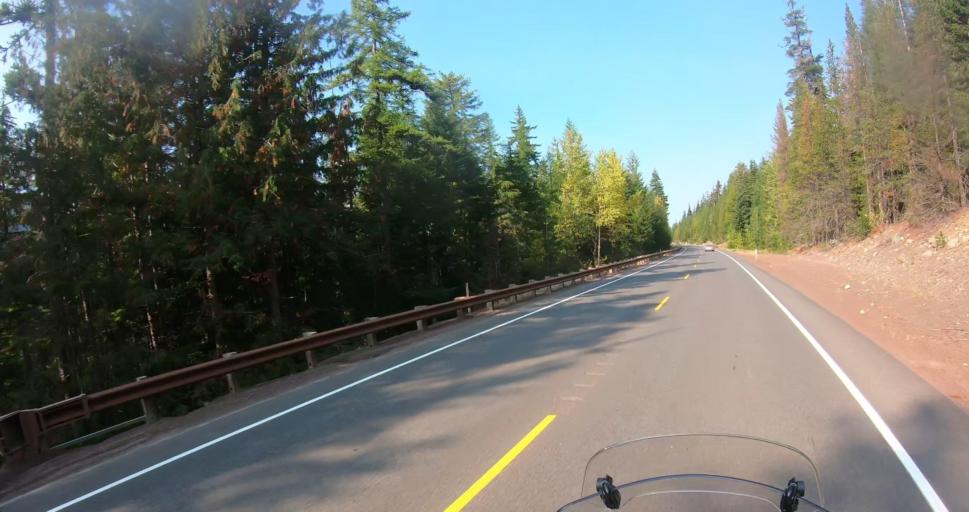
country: US
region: Oregon
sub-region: Hood River County
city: Odell
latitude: 45.3417
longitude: -121.5692
